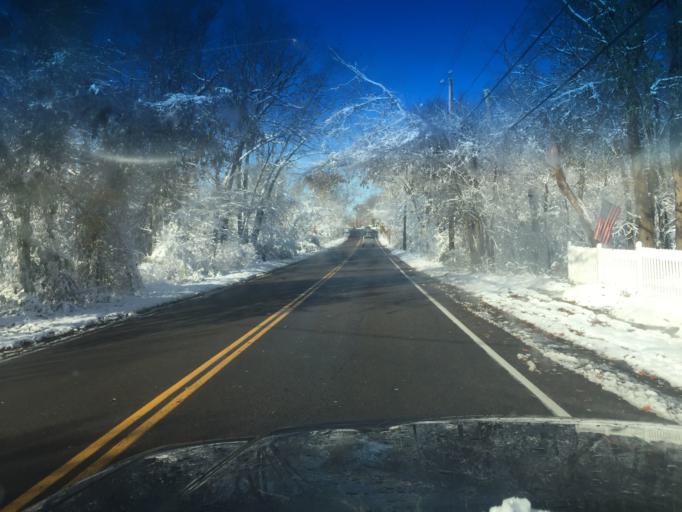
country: US
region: Massachusetts
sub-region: Worcester County
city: Milford
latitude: 42.1466
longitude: -71.4761
